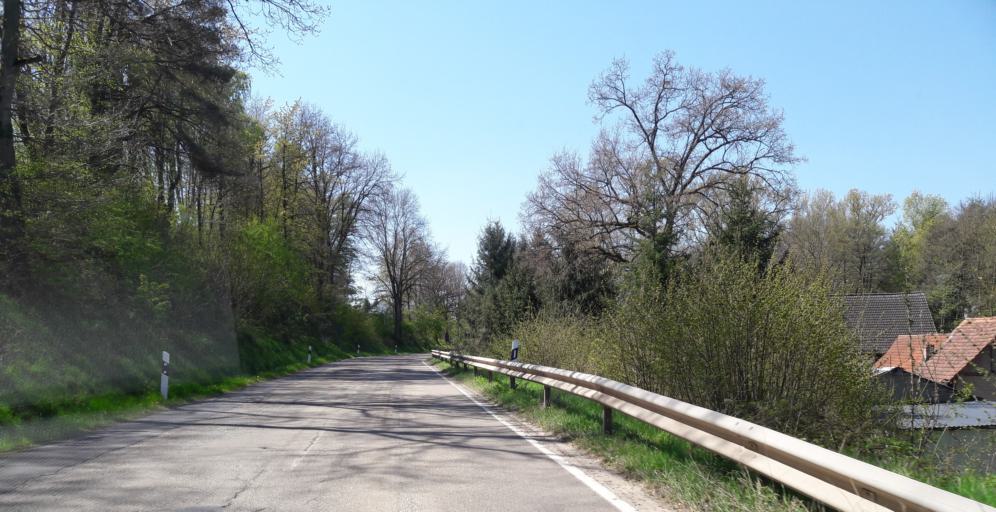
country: DE
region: Rheinland-Pfalz
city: Pfeffelbach
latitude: 49.5430
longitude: 7.3372
